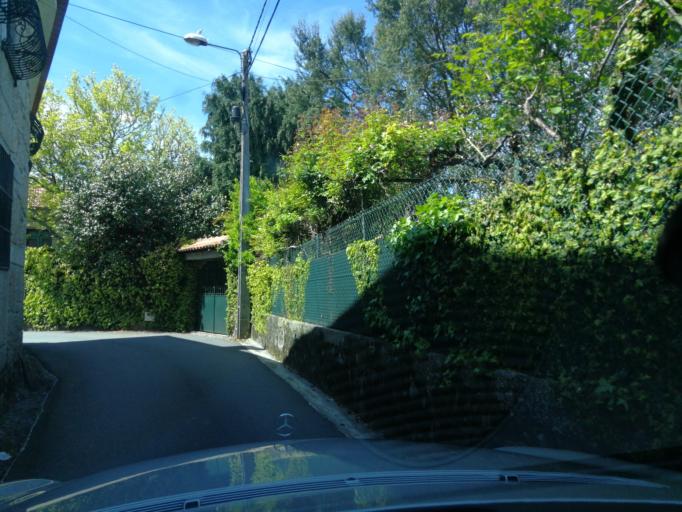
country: PT
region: Braga
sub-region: Vila Nova de Famalicao
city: Calendario
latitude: 41.4312
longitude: -8.5370
